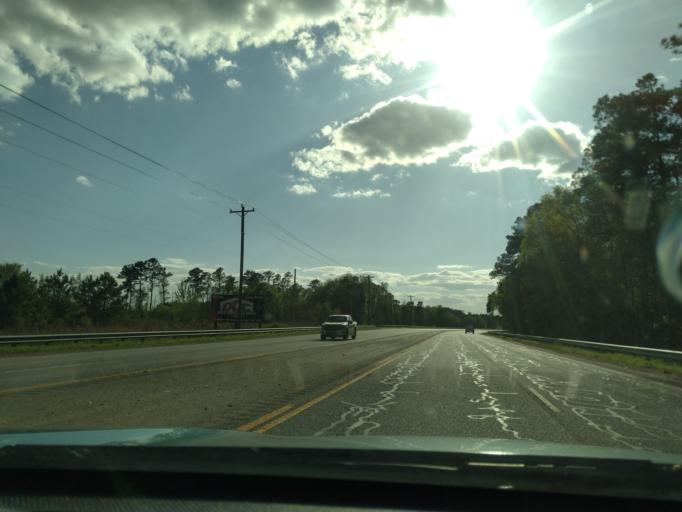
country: US
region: South Carolina
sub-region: Williamsburg County
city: Kingstree
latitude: 33.6586
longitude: -79.8521
